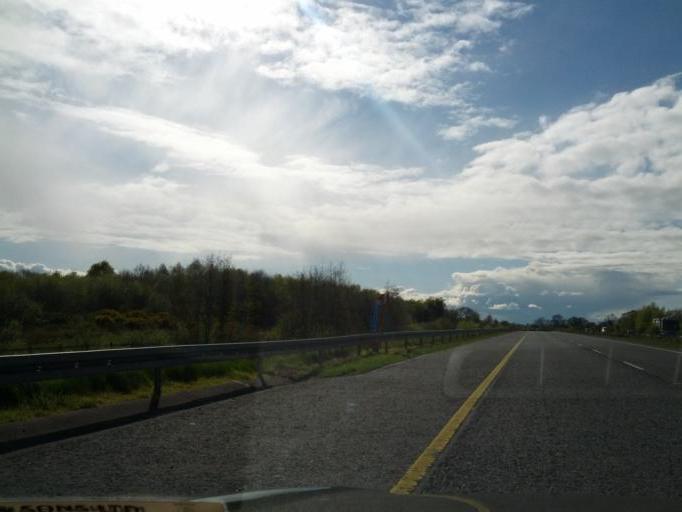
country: IE
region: Leinster
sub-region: An Mhi
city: Longwood
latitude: 53.4257
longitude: -6.9273
